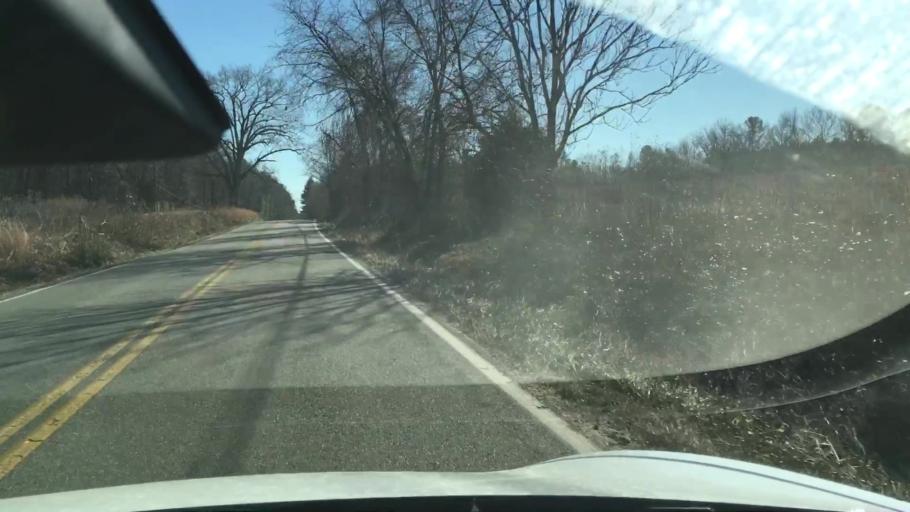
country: US
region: Virginia
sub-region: Henrico County
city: Short Pump
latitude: 37.5764
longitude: -77.7232
